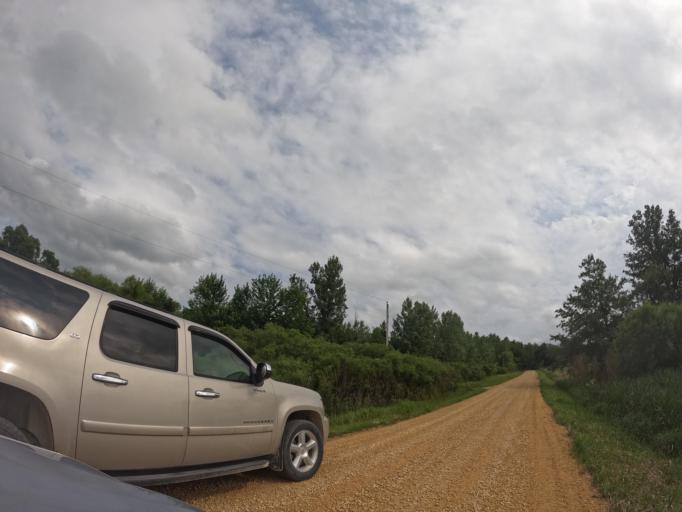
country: US
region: Iowa
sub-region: Clinton County
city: De Witt
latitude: 41.7729
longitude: -90.5829
